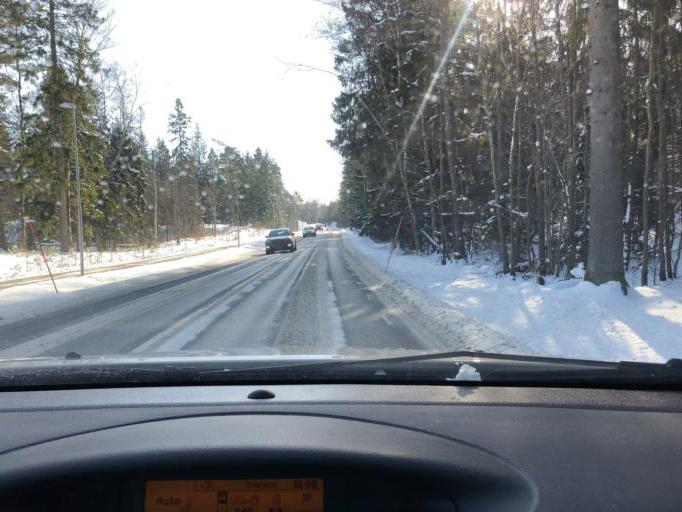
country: SE
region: Stockholm
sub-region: Varmdo Kommun
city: Hemmesta
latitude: 59.2947
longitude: 18.5180
